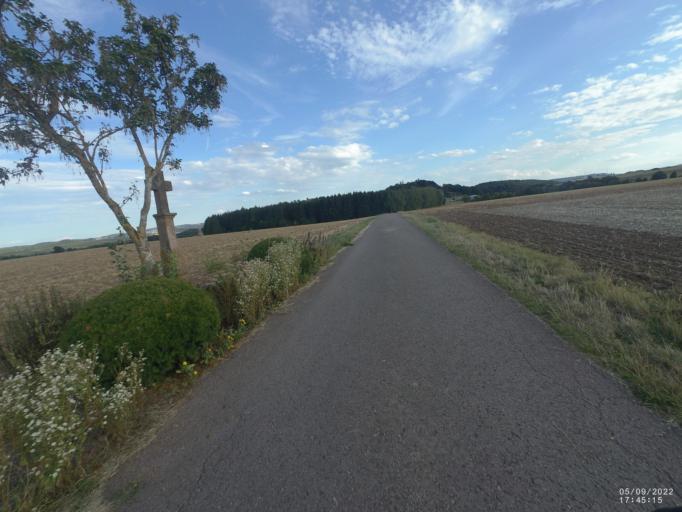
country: DE
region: Rheinland-Pfalz
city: Basberg
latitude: 50.3030
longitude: 6.6016
